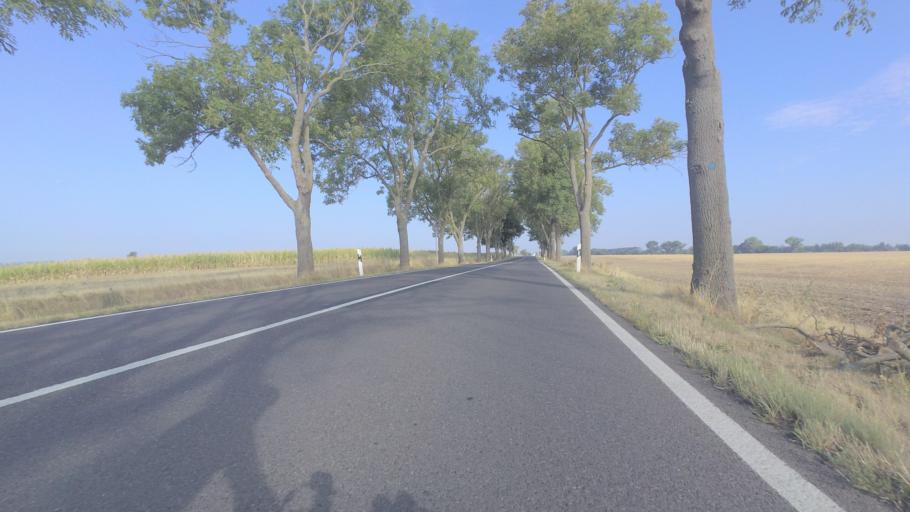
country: DE
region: Brandenburg
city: Kremmen
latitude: 52.7474
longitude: 12.9141
